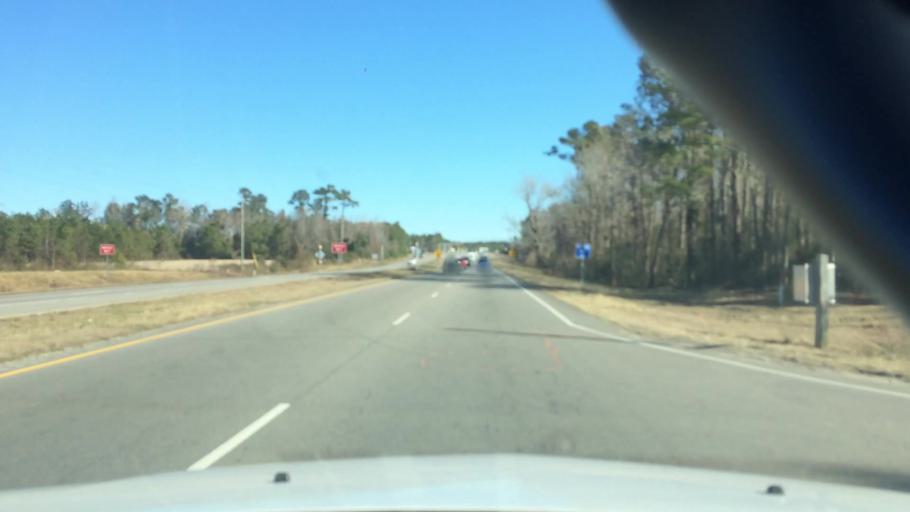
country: US
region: North Carolina
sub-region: Brunswick County
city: Bolivia
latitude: 34.0265
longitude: -78.2609
